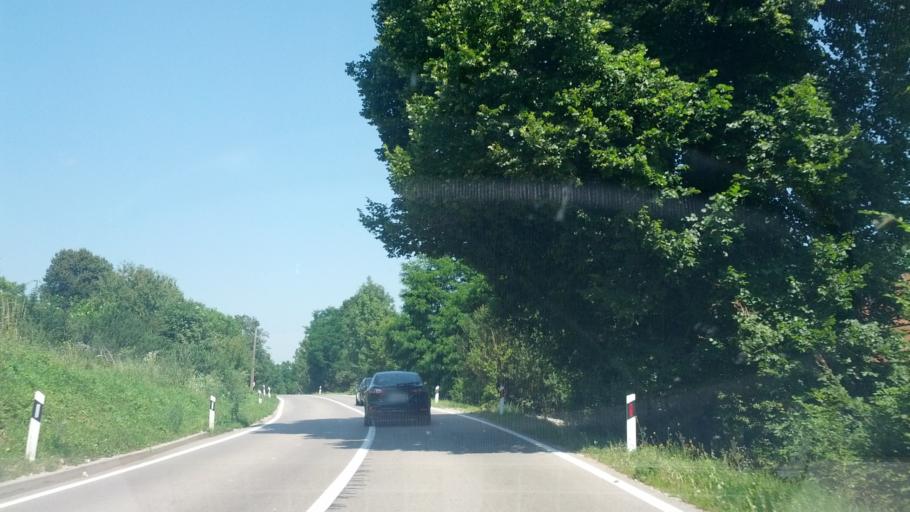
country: BA
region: Federation of Bosnia and Herzegovina
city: Izacic
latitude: 44.8875
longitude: 15.7264
